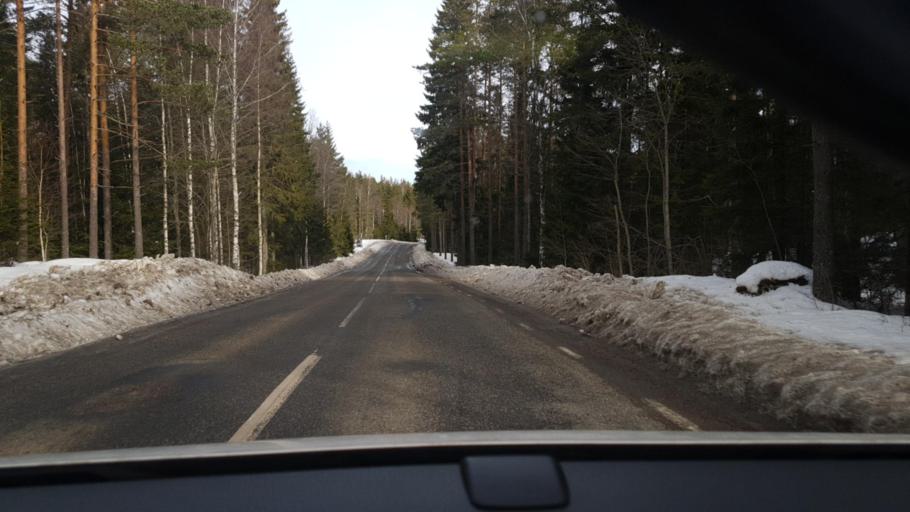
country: SE
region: Vaermland
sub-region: Eda Kommun
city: Amotfors
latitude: 59.5943
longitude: 12.2982
